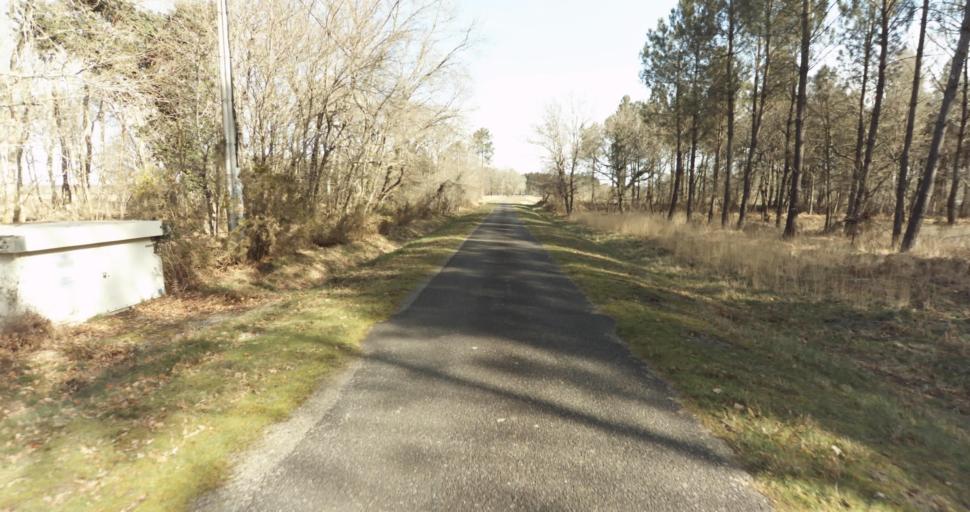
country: FR
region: Aquitaine
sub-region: Departement des Landes
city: Roquefort
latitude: 44.0982
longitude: -0.3167
